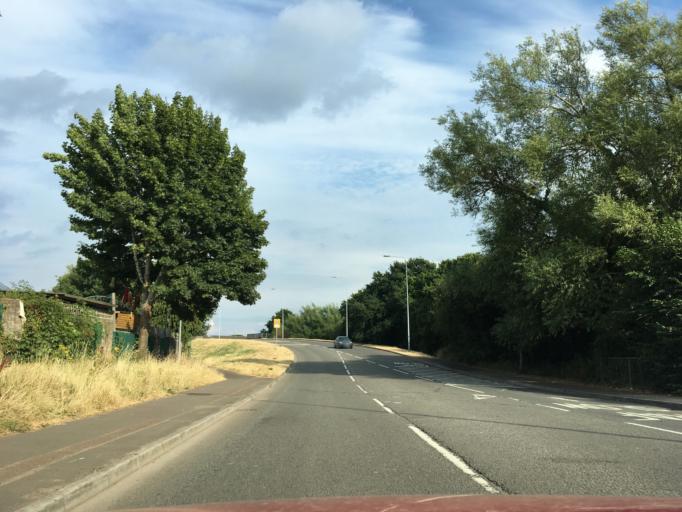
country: GB
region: Wales
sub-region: Newport
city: Marshfield
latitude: 51.5178
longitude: -3.1012
